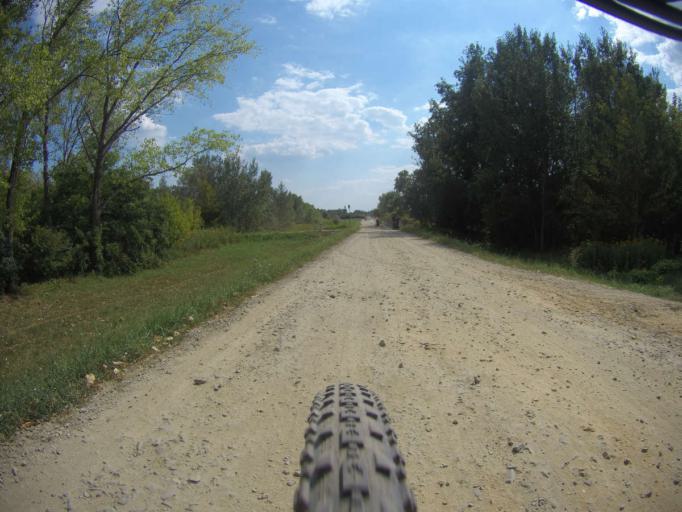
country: HU
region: Pest
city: Budakalasz
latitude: 47.6263
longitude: 19.0849
